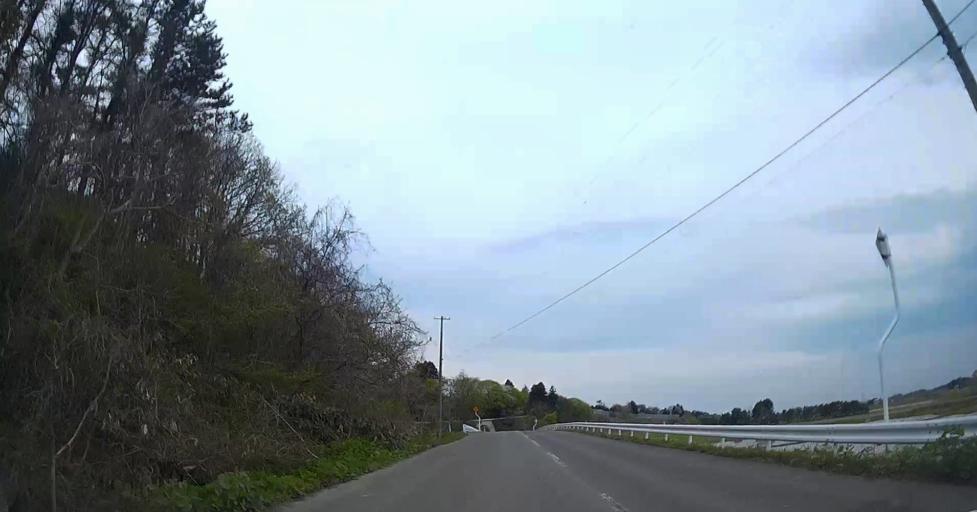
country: JP
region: Aomori
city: Goshogawara
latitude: 40.8997
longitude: 140.4914
